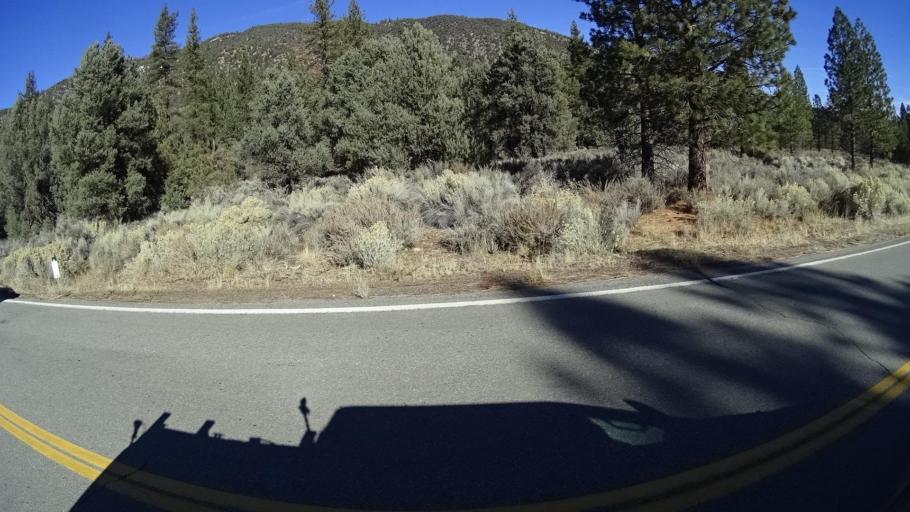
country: US
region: California
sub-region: Kern County
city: Pine Mountain Club
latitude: 34.8534
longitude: -119.1810
